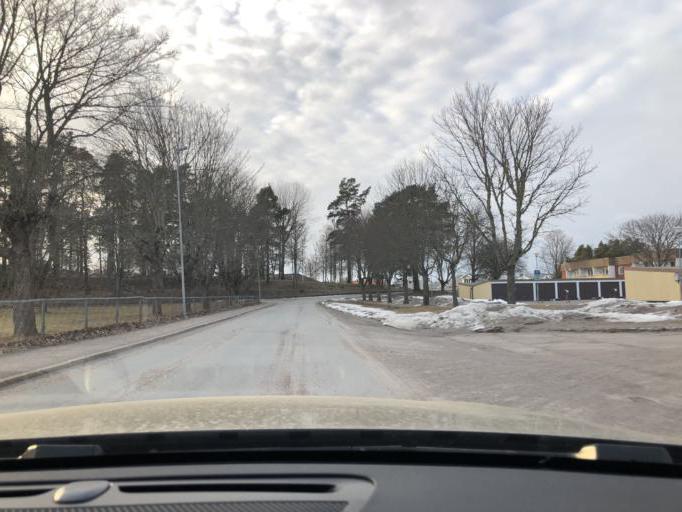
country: SE
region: Uppsala
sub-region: Tierps Kommun
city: Tierp
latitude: 60.3381
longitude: 17.5134
